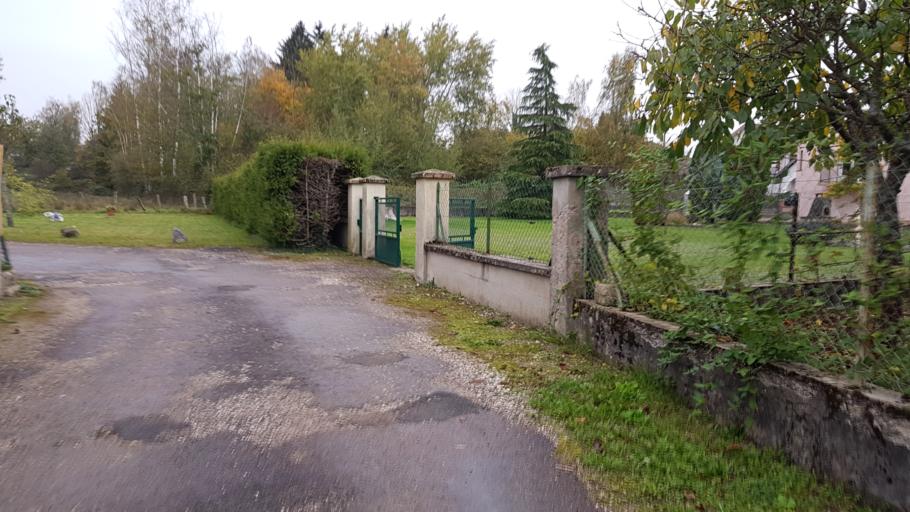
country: FR
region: Franche-Comte
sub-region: Departement de la Haute-Saone
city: Luxeuil-les-Bains
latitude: 47.8190
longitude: 6.3730
